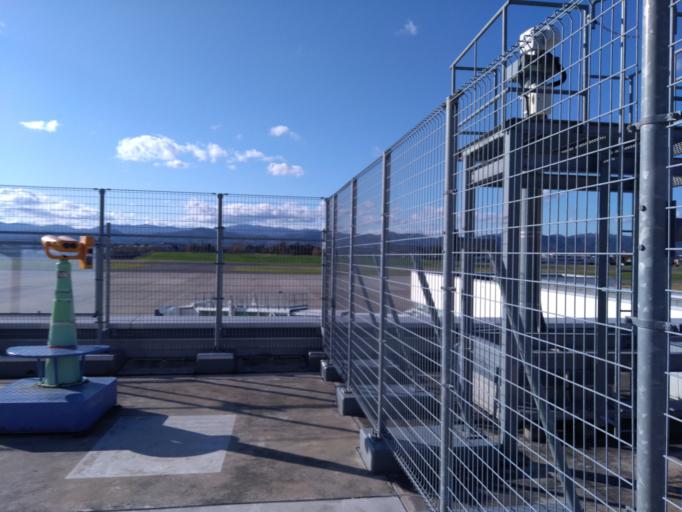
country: JP
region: Iwate
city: Hanamaki
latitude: 39.4217
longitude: 141.1384
